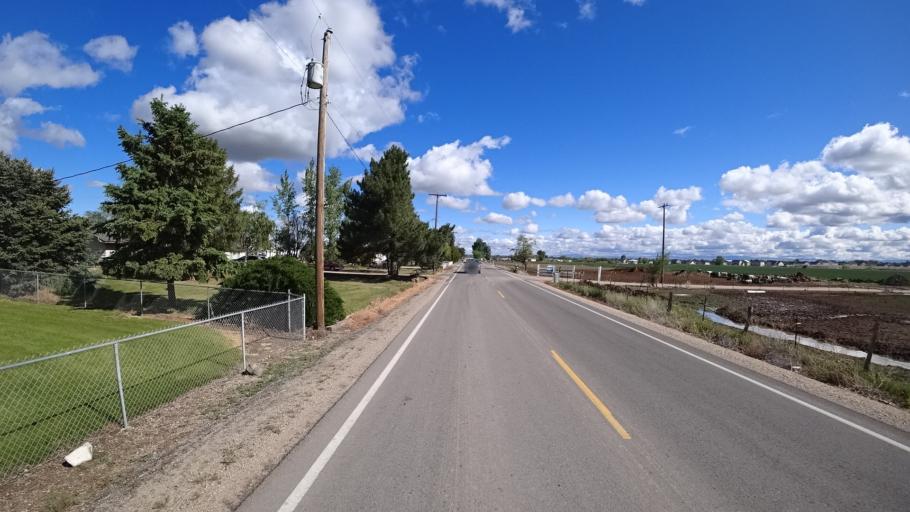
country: US
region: Idaho
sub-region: Ada County
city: Kuna
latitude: 43.4992
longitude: -116.4537
